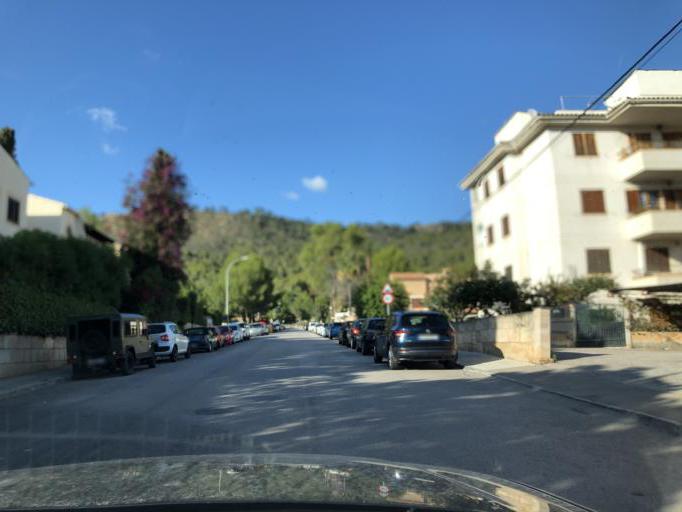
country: ES
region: Balearic Islands
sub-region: Illes Balears
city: Camp de Mar
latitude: 39.5382
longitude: 2.4394
